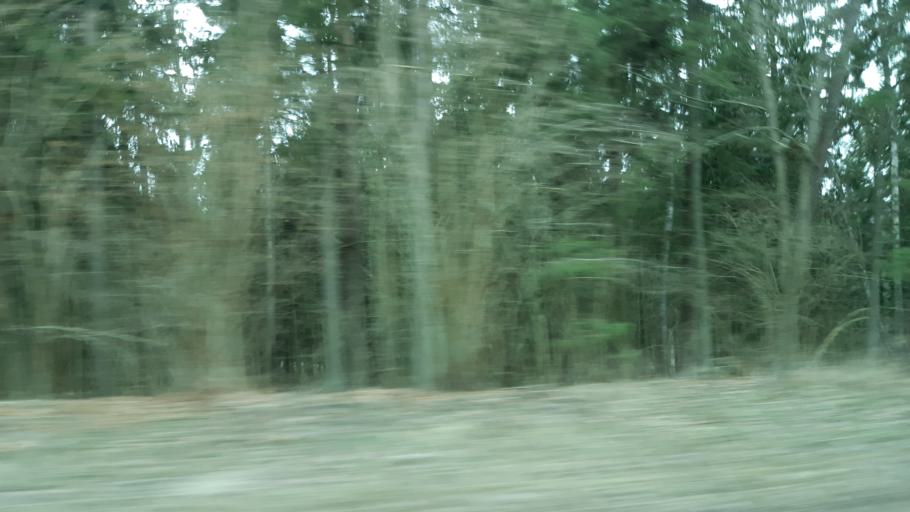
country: PL
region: Podlasie
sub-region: Suwalki
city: Suwalki
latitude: 54.2825
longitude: 22.9483
